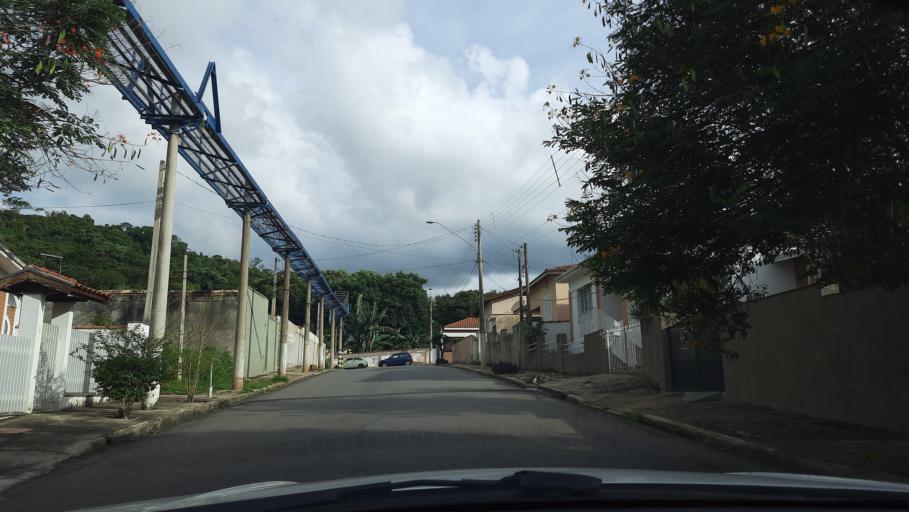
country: BR
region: Sao Paulo
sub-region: Sao Joao Da Boa Vista
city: Sao Joao da Boa Vista
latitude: -21.9451
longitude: -46.7150
